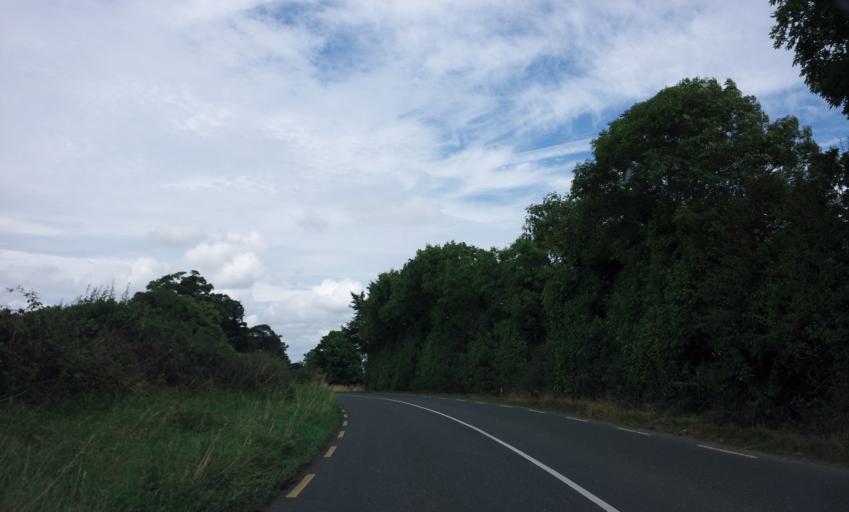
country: IE
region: Leinster
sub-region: Laois
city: Stradbally
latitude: 52.9747
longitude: -7.2133
